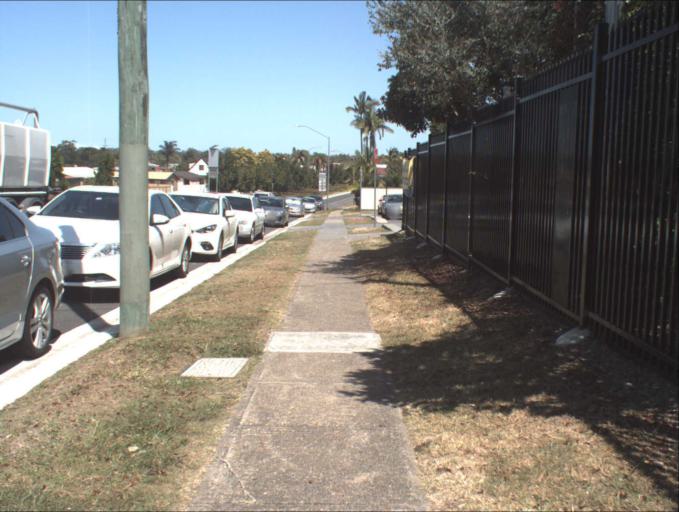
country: AU
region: Queensland
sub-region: Logan
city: Windaroo
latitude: -27.7266
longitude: 153.2062
